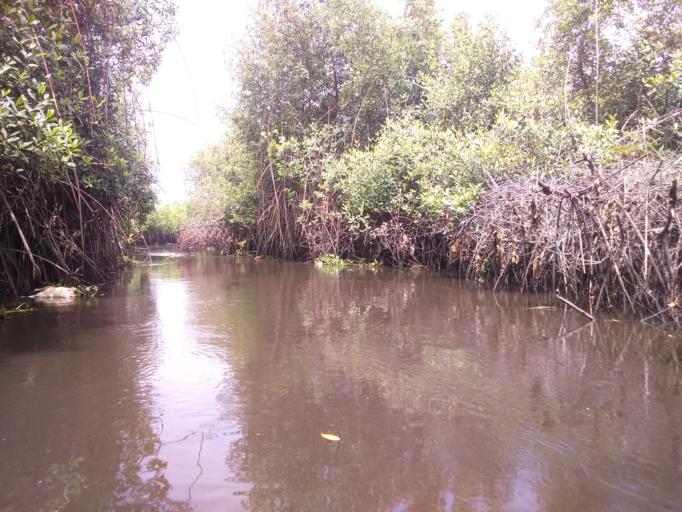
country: BJ
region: Mono
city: Grand-Popo
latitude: 6.3108
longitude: 1.9166
